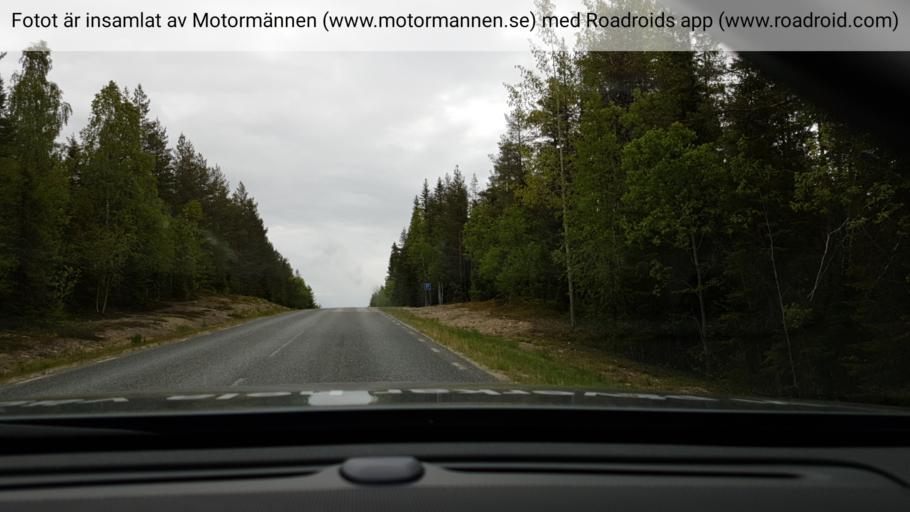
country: SE
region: Vaesterbotten
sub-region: Asele Kommun
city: Insjon
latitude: 64.3497
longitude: 17.8426
